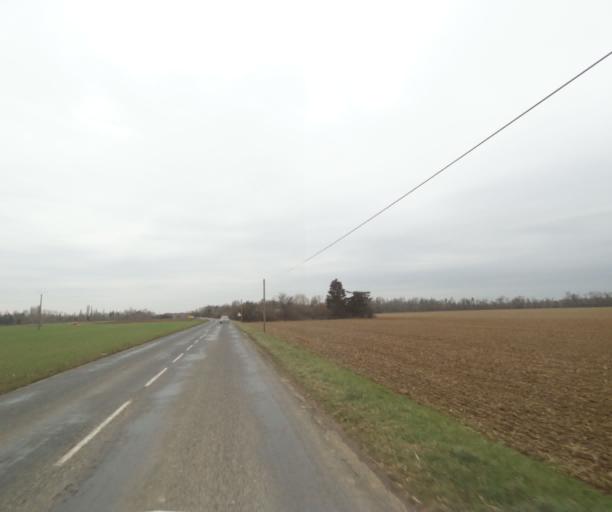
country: FR
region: Champagne-Ardenne
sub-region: Departement de la Haute-Marne
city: Villiers-en-Lieu
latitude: 48.6538
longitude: 4.9081
